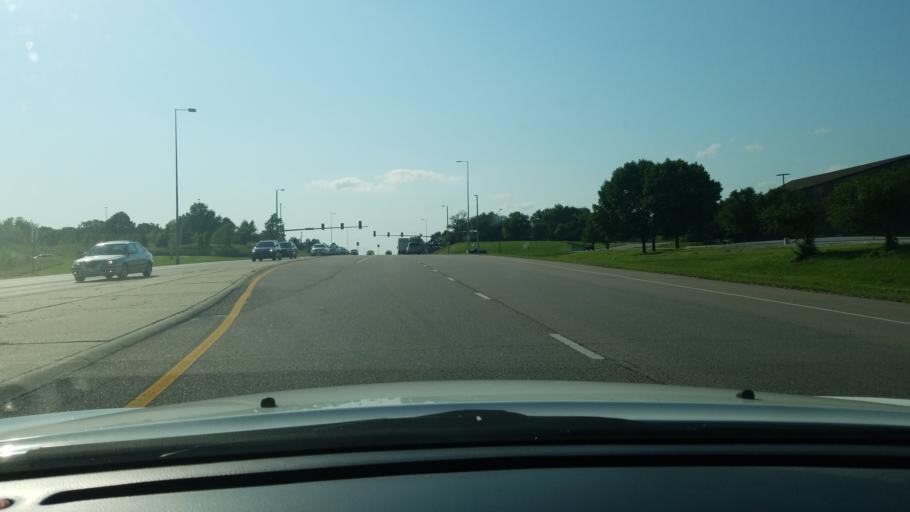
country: US
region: Nebraska
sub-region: Lancaster County
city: Lincoln
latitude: 40.7451
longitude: -96.6232
